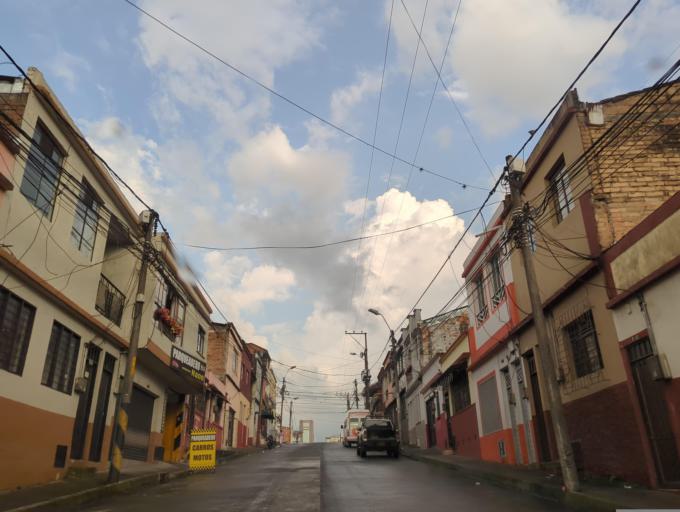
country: CO
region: Risaralda
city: Pereira
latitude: 4.8132
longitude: -75.7027
